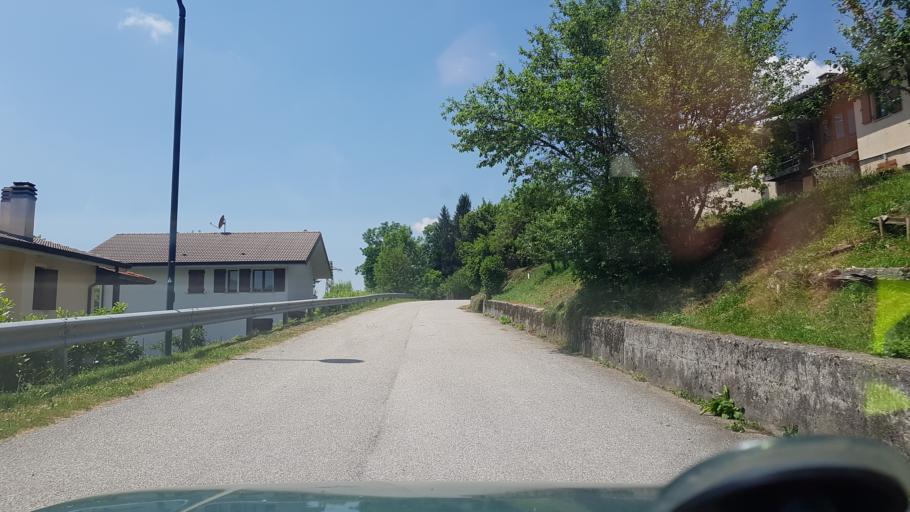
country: IT
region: Friuli Venezia Giulia
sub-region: Provincia di Udine
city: Lusevera
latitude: 46.2725
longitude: 13.3074
